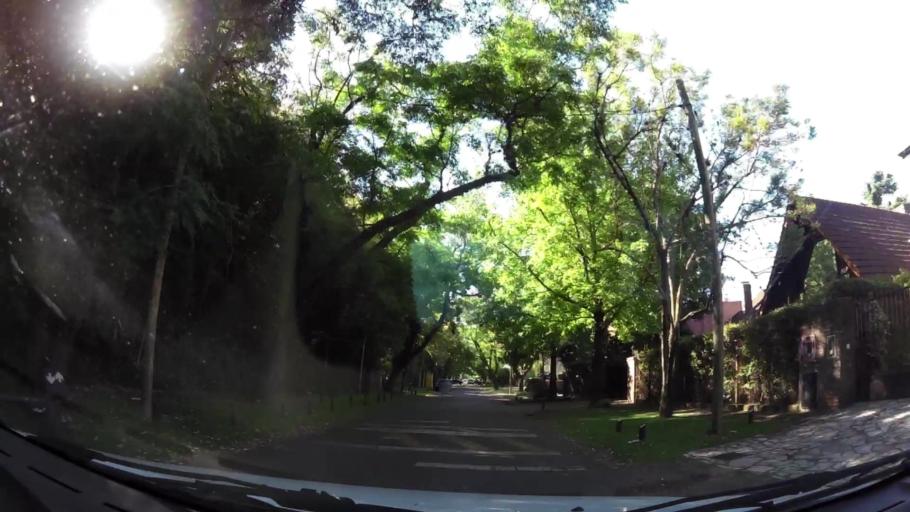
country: AR
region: Buenos Aires
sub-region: Partido de San Isidro
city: San Isidro
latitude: -34.4831
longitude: -58.5418
